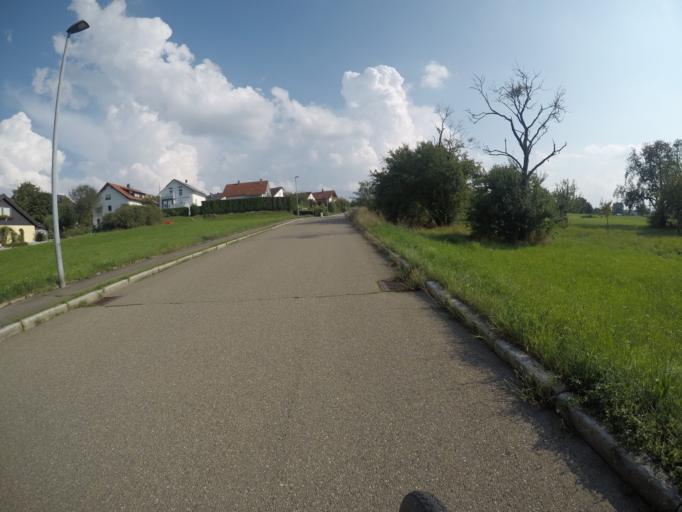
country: DE
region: Baden-Wuerttemberg
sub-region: Tuebingen Region
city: Pliezhausen
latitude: 48.5591
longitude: 9.2322
